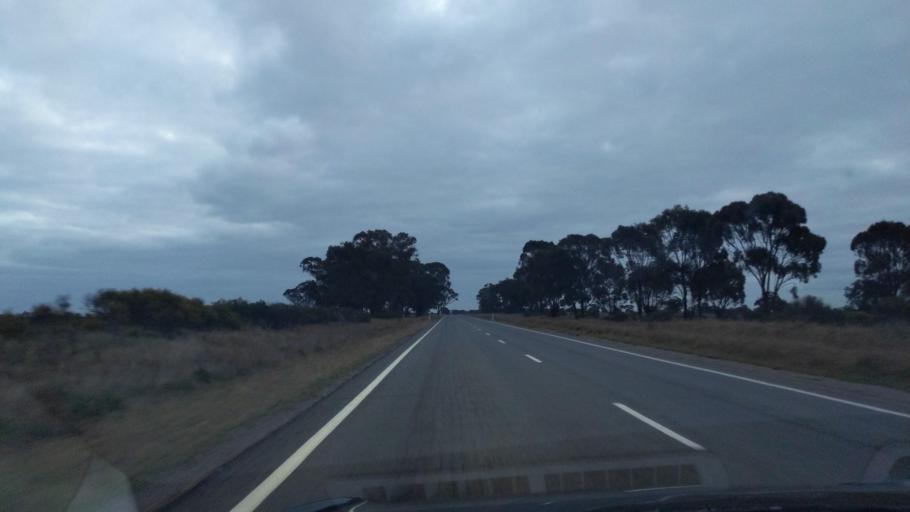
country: AU
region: New South Wales
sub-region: Coolamon
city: Coolamon
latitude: -34.7607
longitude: 146.8850
